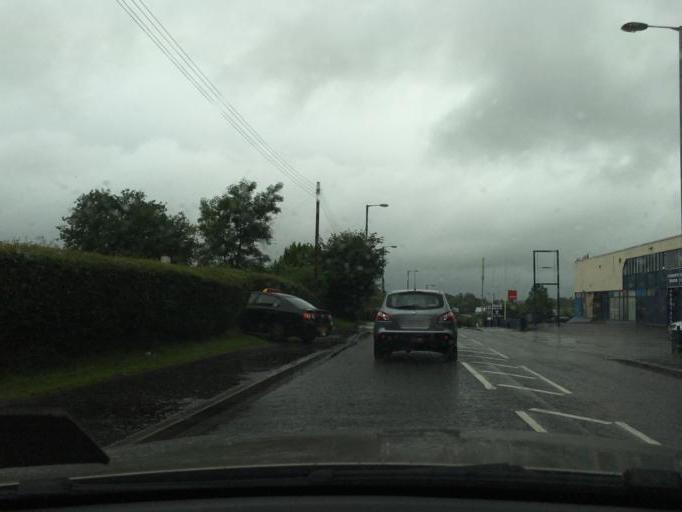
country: GB
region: Northern Ireland
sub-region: Fermanagh District
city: Enniskillen
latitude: 54.3536
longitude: -7.6367
